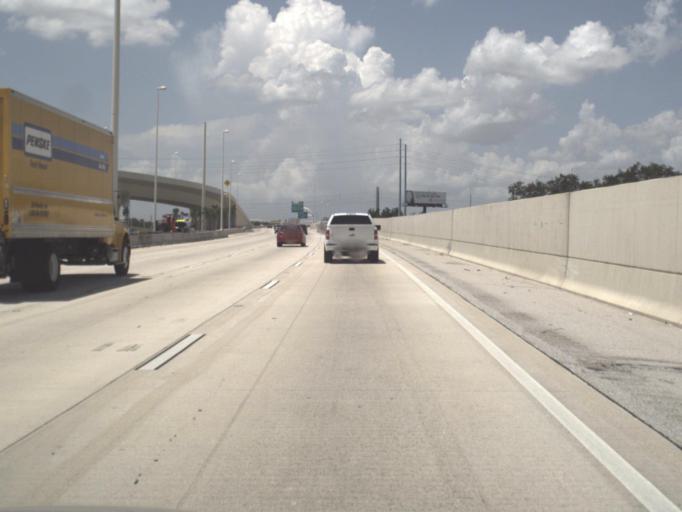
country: US
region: Florida
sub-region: Hillsborough County
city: Tampa
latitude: 27.9656
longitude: -82.4248
